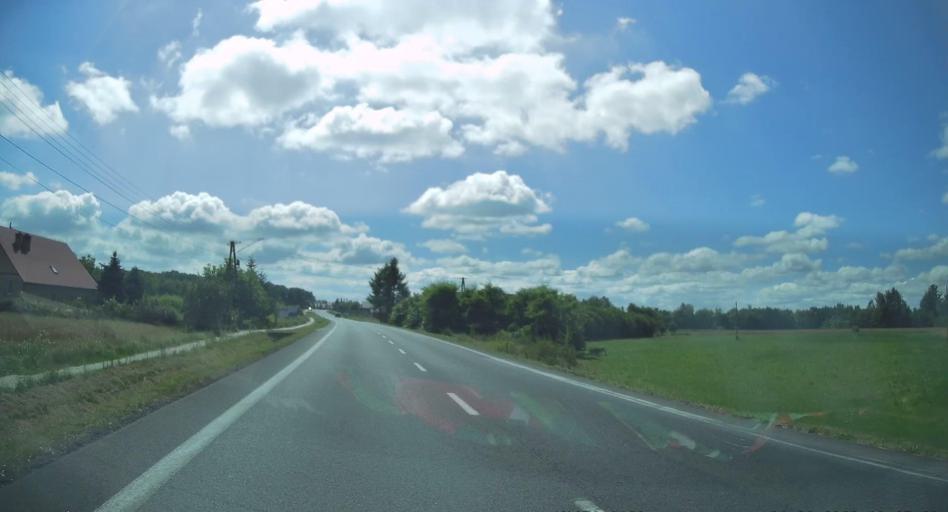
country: PL
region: Subcarpathian Voivodeship
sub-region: Powiat debicki
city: Brzeznica
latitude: 50.1250
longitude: 21.4864
